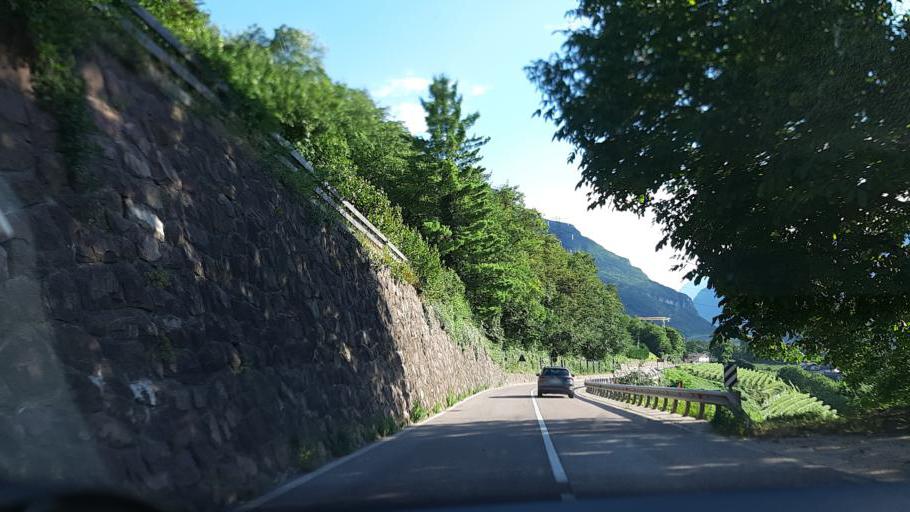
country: IT
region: Trentino-Alto Adige
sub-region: Bolzano
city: Egna
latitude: 46.3218
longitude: 11.2874
